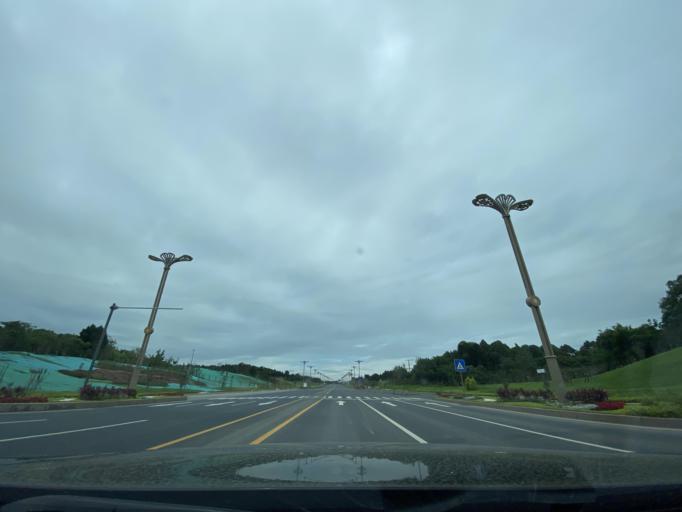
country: CN
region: Sichuan
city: Jiancheng
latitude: 30.3087
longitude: 104.3562
